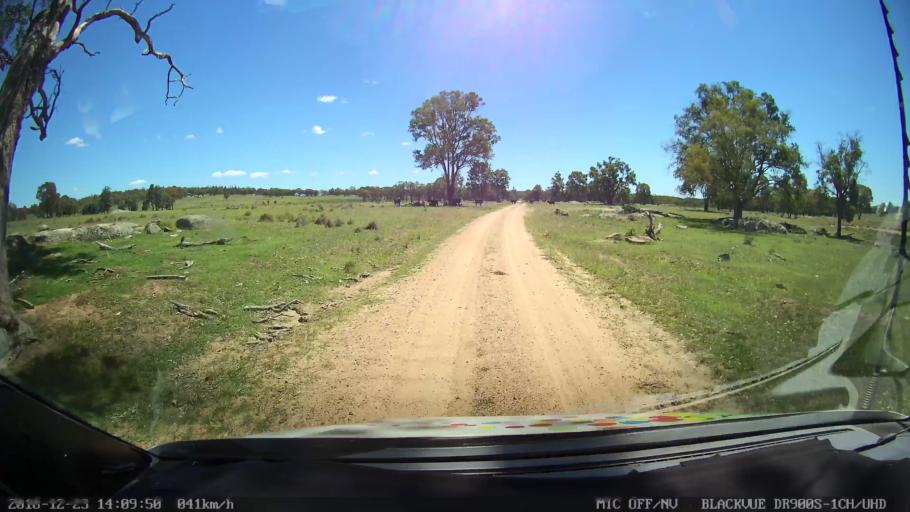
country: AU
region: New South Wales
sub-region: Tamworth Municipality
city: Manilla
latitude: -30.6472
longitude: 151.0595
